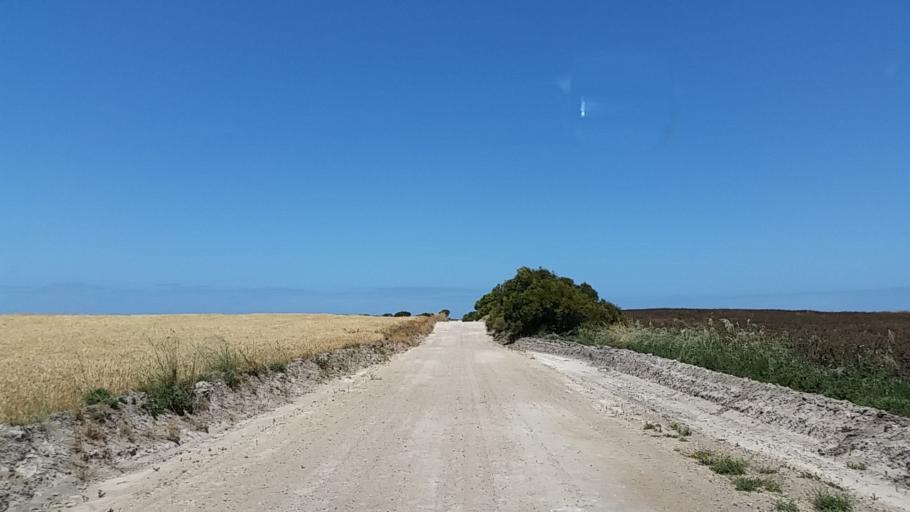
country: AU
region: South Australia
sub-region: Yorke Peninsula
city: Honiton
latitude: -35.2335
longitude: 137.1256
